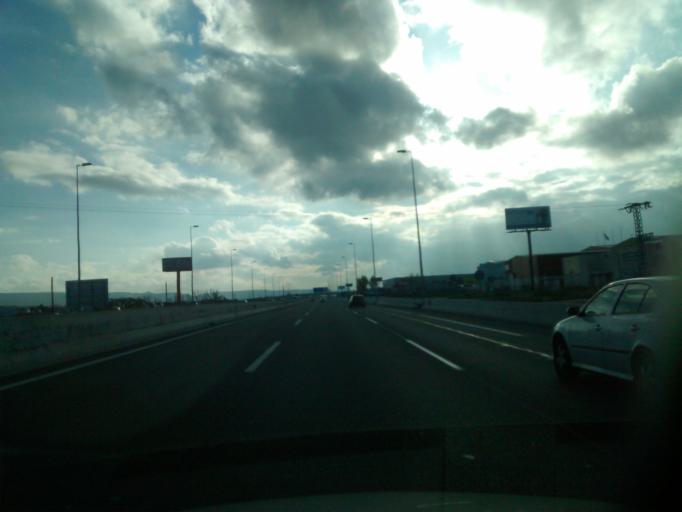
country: ES
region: Castille-La Mancha
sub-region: Provincia de Guadalajara
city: Alovera
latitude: 40.6008
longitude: -3.2178
